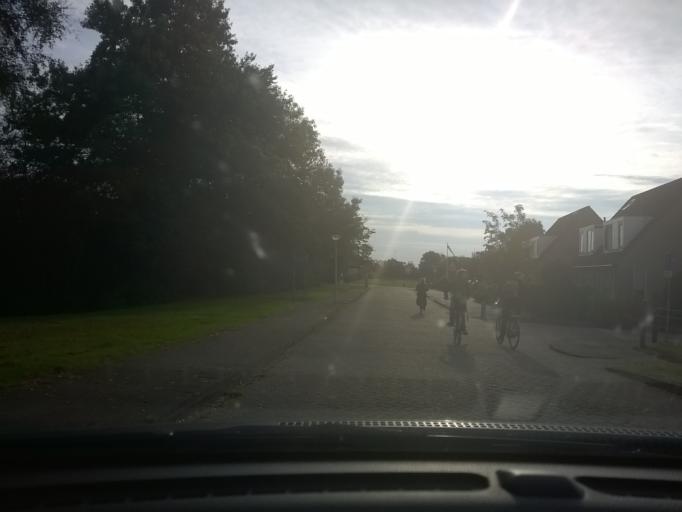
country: NL
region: Friesland
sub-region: Gemeente Heerenveen
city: Heerenveen
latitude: 52.9659
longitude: 5.9089
